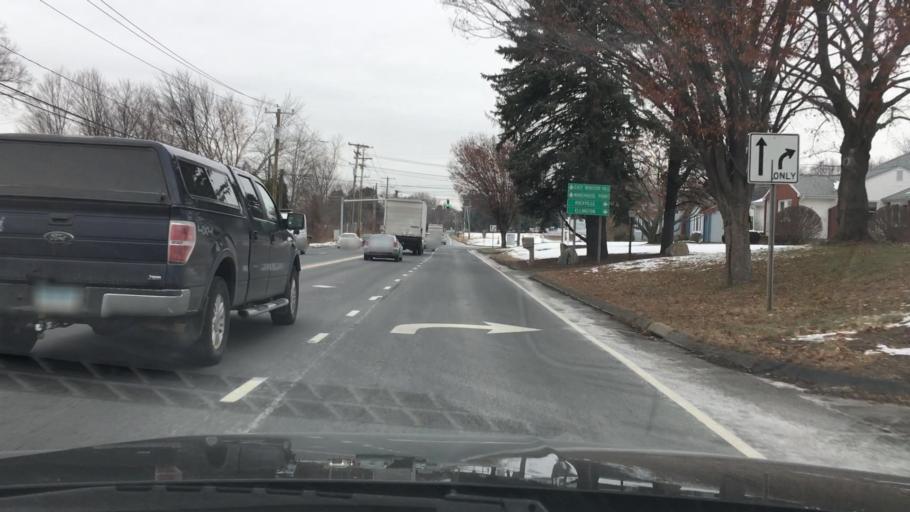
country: US
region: Connecticut
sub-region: Hartford County
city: Manchester
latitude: 41.8298
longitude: -72.5546
